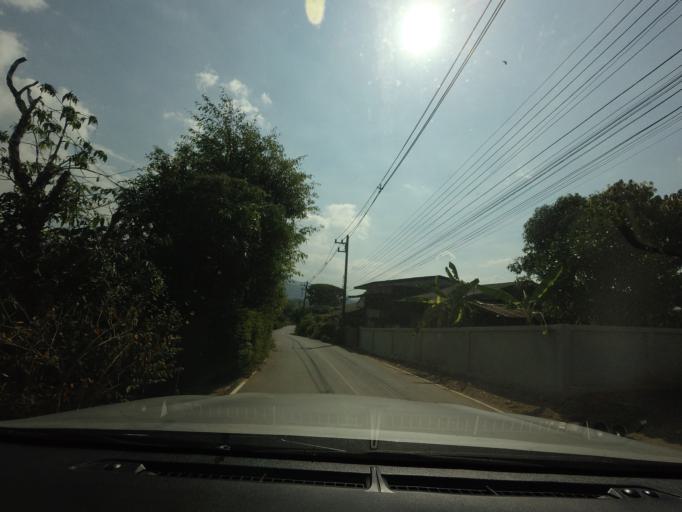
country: TH
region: Mae Hong Son
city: Wiang Nuea
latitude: 19.3983
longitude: 98.4429
